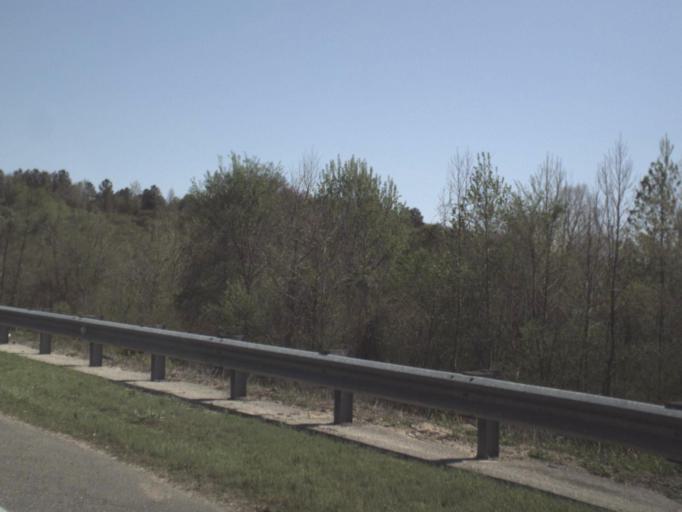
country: US
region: Florida
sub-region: Liberty County
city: Bristol
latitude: 30.4323
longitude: -84.9963
